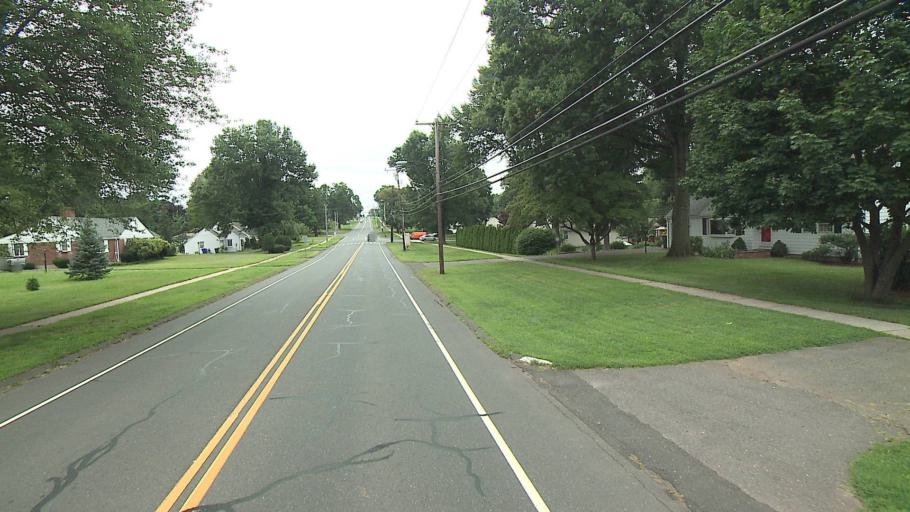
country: US
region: Connecticut
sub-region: Hartford County
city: Wethersfield
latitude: 41.6816
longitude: -72.6650
